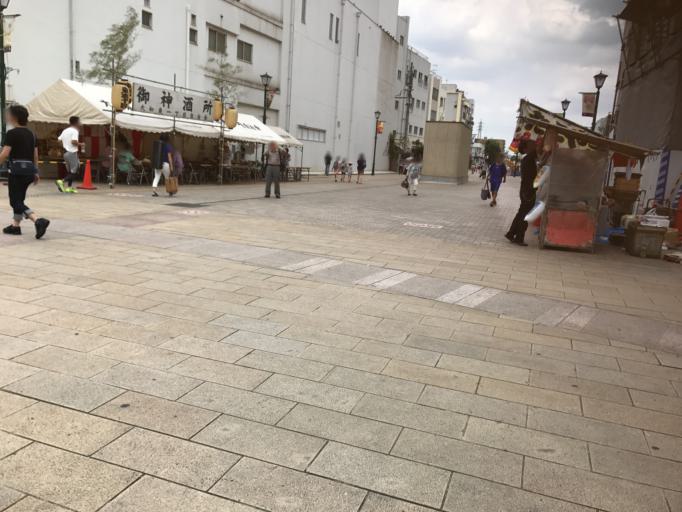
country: JP
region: Kanagawa
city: Minami-rinkan
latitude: 35.4699
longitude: 139.4620
